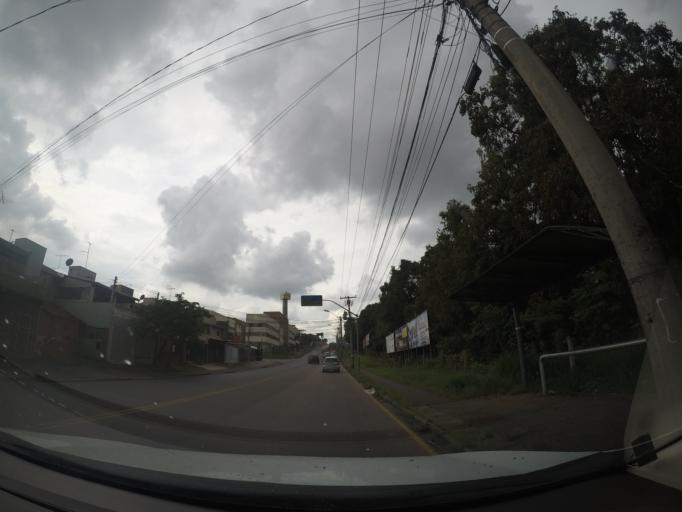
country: BR
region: Parana
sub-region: Sao Jose Dos Pinhais
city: Sao Jose dos Pinhais
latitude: -25.5248
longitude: -49.2468
